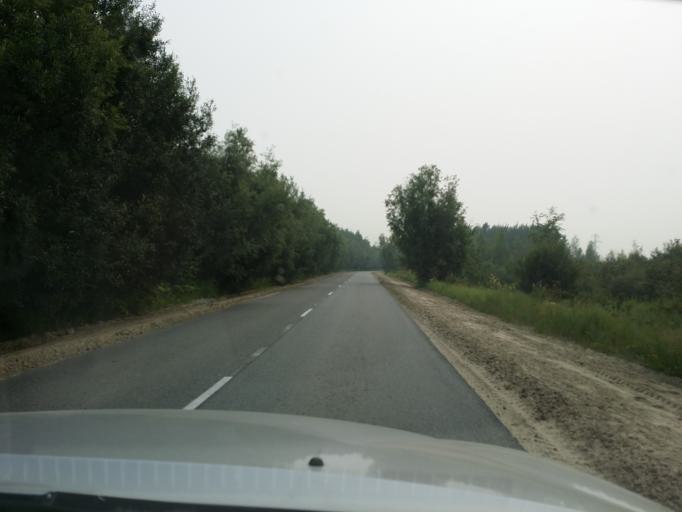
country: RU
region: Khanty-Mansiyskiy Avtonomnyy Okrug
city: Megion
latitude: 60.9949
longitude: 76.3011
